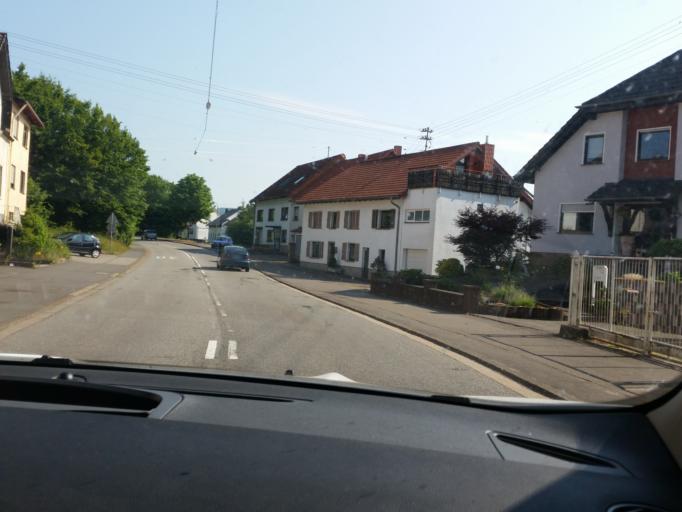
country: DE
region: Saarland
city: Schmelz
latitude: 49.4271
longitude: 6.8469
